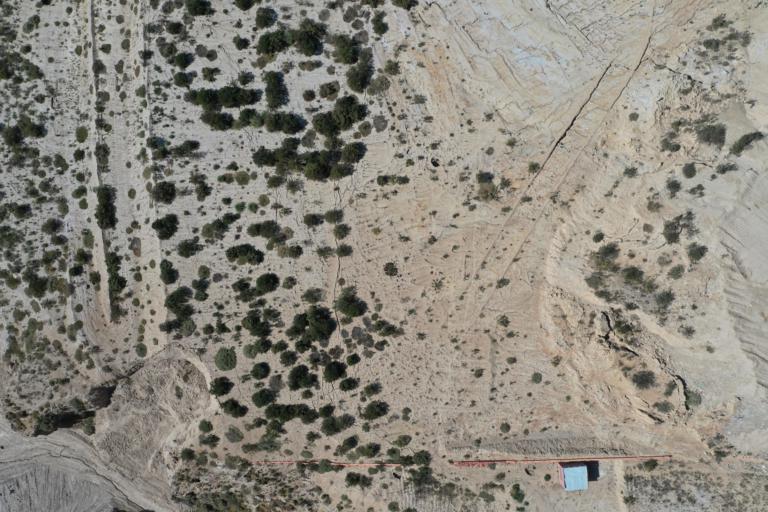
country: BO
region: La Paz
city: La Paz
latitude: -16.5508
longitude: -68.1260
